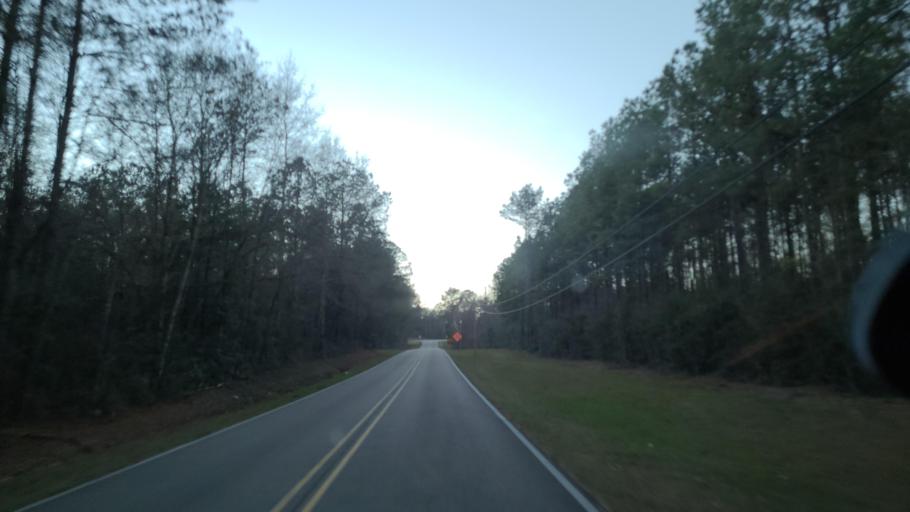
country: US
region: Mississippi
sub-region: Forrest County
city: Hattiesburg
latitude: 31.1676
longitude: -89.2398
